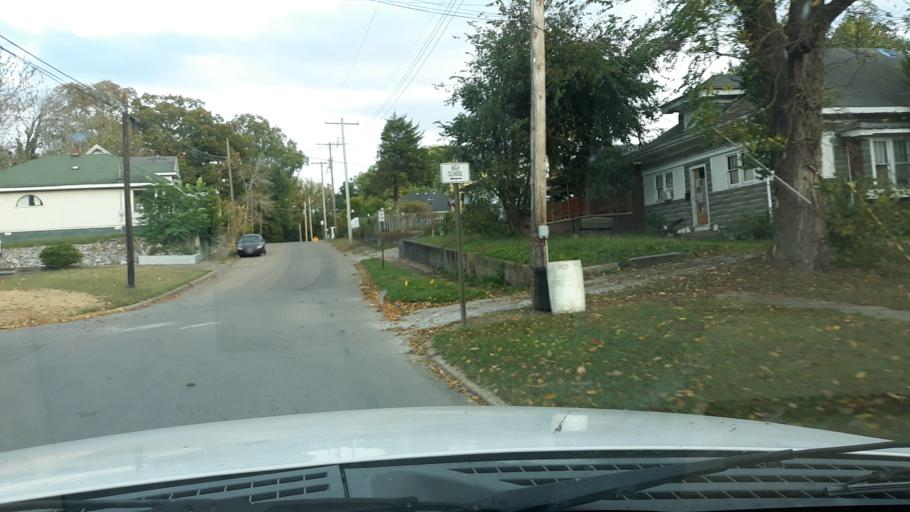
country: US
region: Illinois
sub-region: Saline County
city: Eldorado
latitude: 37.8162
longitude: -88.4352
